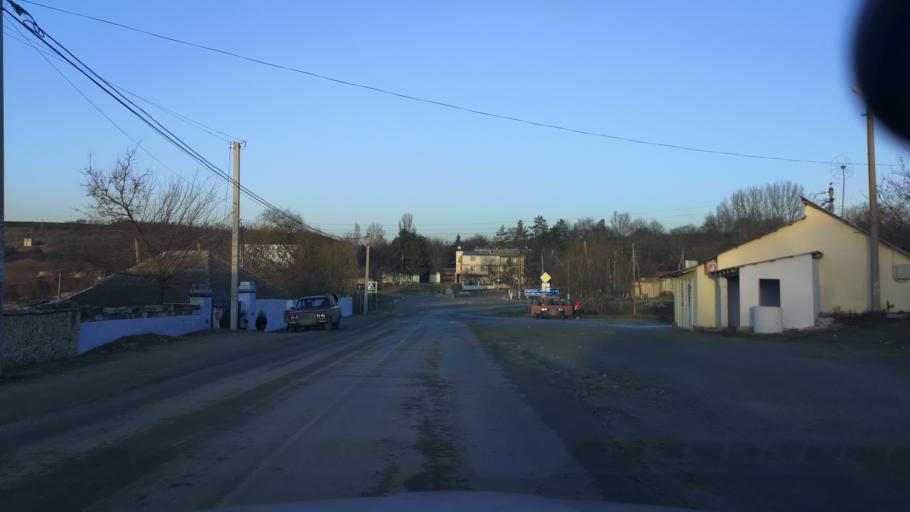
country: MD
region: Orhei
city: Orhei
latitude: 47.3089
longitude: 28.9310
